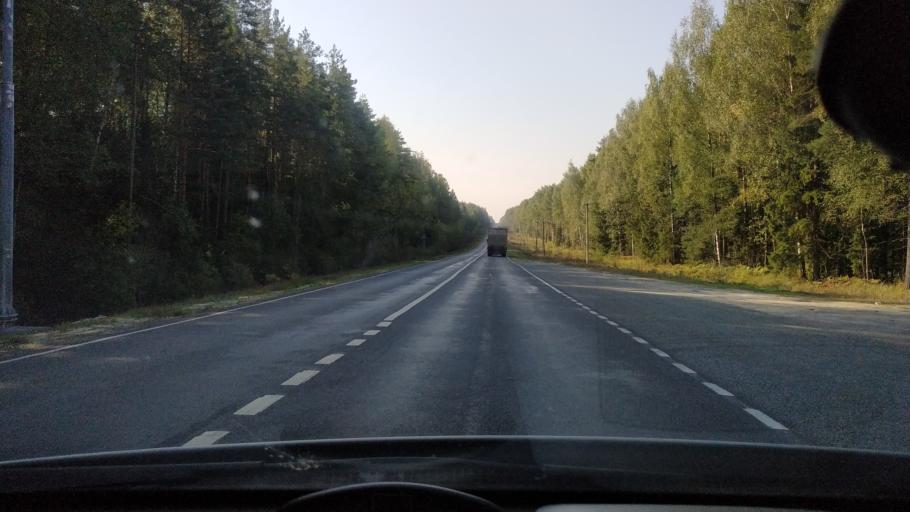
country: RU
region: Moskovskaya
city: Tugolesskiy Bor
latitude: 55.5042
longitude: 39.7132
